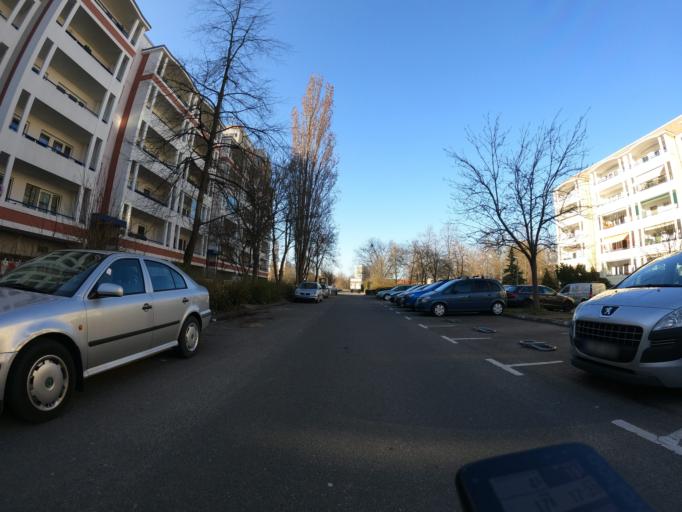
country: DE
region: Berlin
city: Marzahn
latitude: 52.5400
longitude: 13.5581
